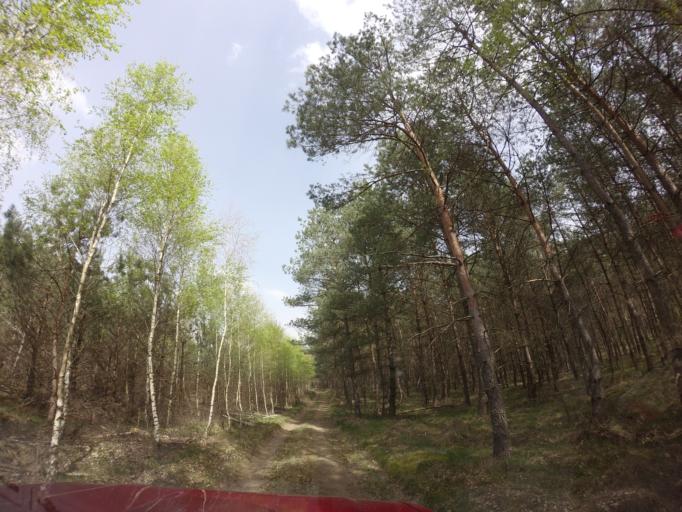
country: PL
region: West Pomeranian Voivodeship
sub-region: Powiat choszczenski
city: Drawno
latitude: 53.2740
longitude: 15.7103
